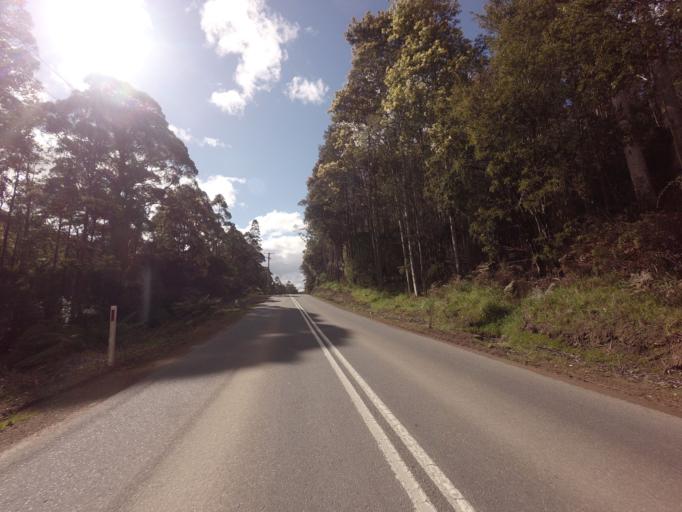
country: AU
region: Tasmania
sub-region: Huon Valley
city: Geeveston
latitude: -43.2295
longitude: 146.9882
